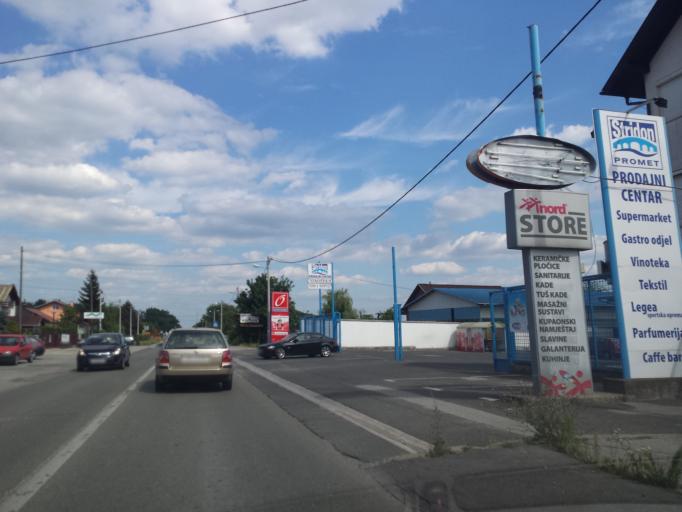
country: HR
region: Grad Zagreb
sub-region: Sesvete
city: Sesvete
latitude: 45.8143
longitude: 16.1850
